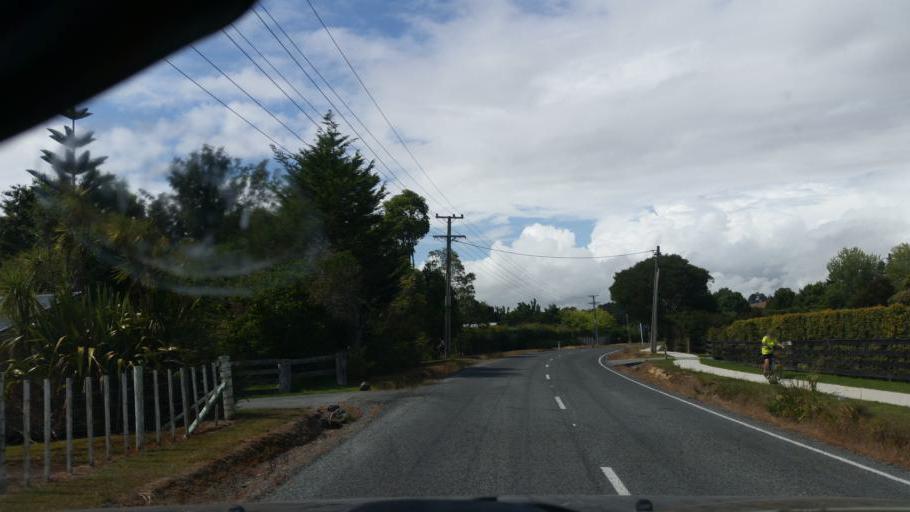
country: NZ
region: Auckland
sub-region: Auckland
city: Wellsford
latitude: -36.1246
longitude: 174.5586
